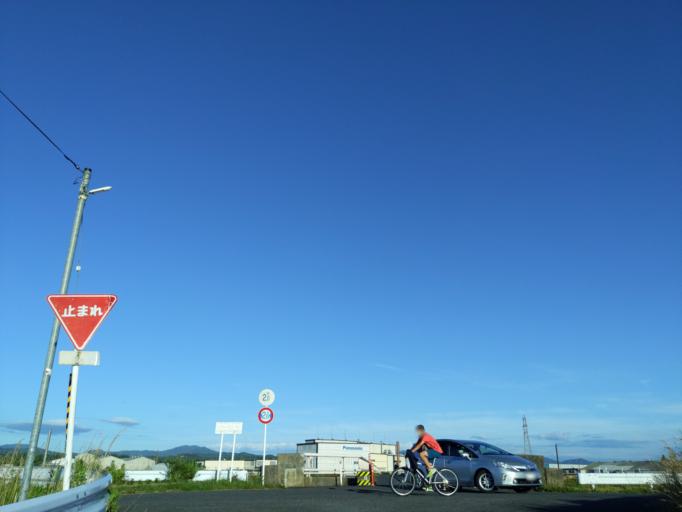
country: JP
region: Fukushima
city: Koriyama
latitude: 37.3815
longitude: 140.3917
